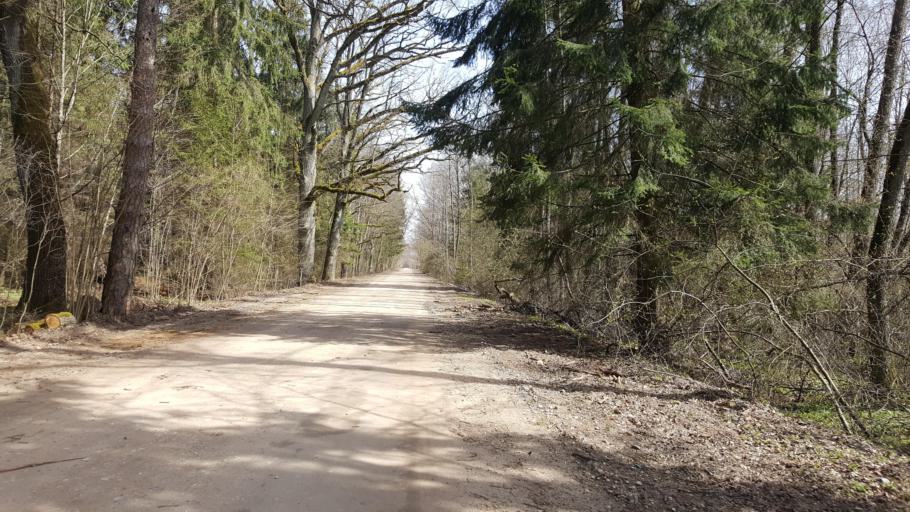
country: BY
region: Brest
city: Kamyanyuki
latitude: 52.5507
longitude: 23.6639
